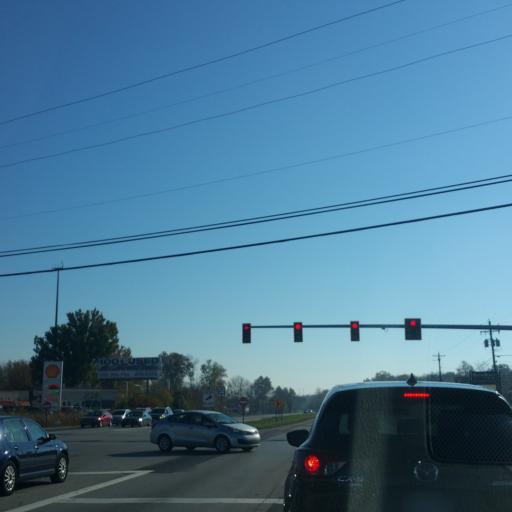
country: US
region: Ohio
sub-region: Clermont County
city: Summerside
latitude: 39.0909
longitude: -84.2487
